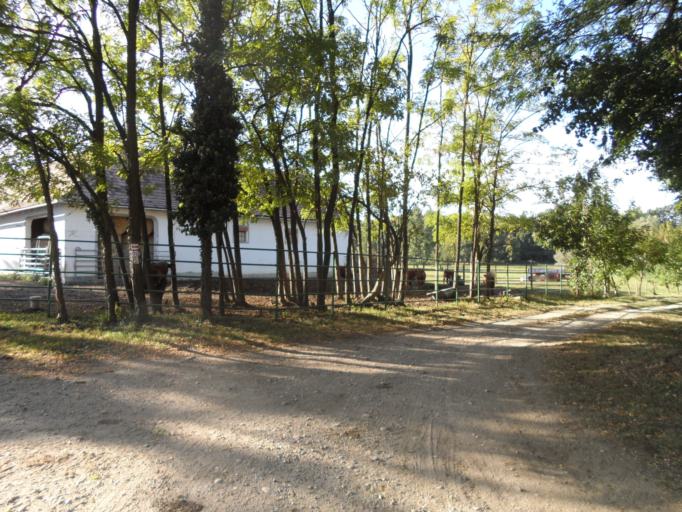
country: HU
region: Veszprem
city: Papa
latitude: 47.2687
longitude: 17.5156
